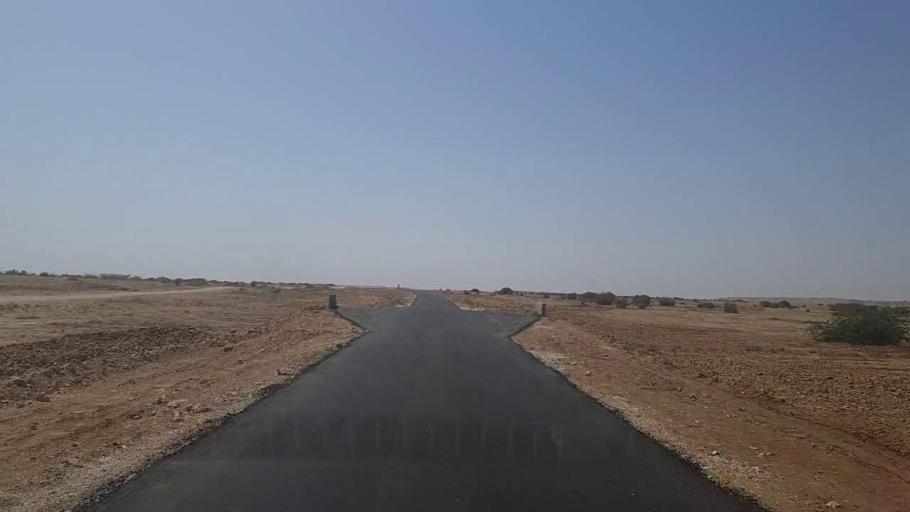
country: PK
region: Sindh
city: Kotri
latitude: 25.1488
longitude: 68.2100
